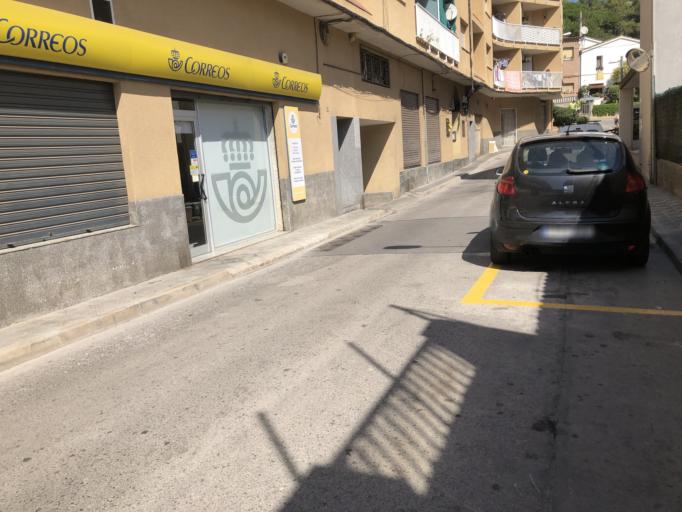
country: ES
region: Catalonia
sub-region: Provincia de Barcelona
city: Torrelles de Llobregat
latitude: 41.3584
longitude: 1.9805
